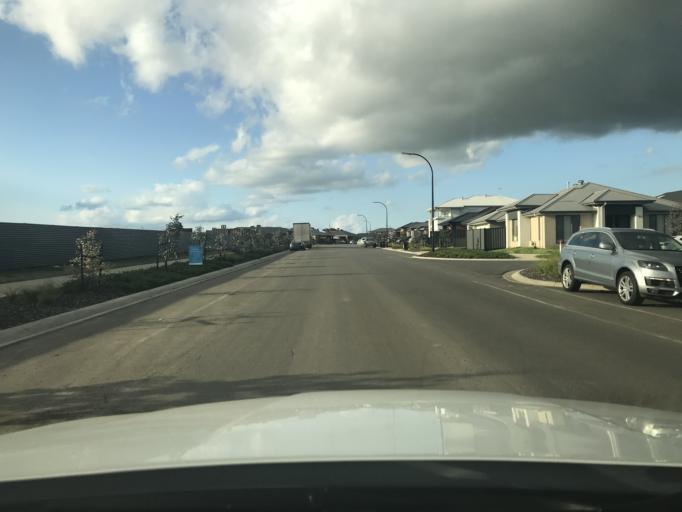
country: AU
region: Victoria
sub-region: Hume
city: Craigieburn
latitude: -37.5737
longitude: 144.9005
